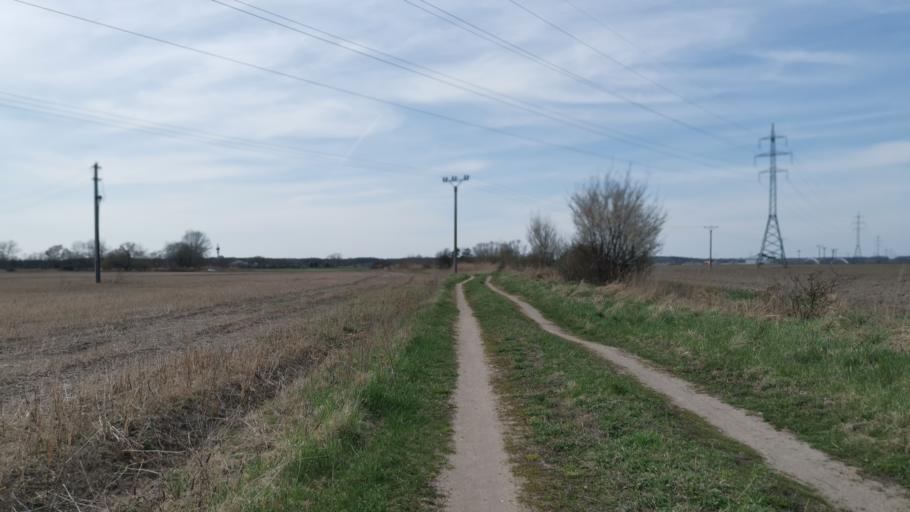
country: CZ
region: South Moravian
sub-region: Okres Breclav
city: Lanzhot
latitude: 48.6946
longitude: 17.0314
